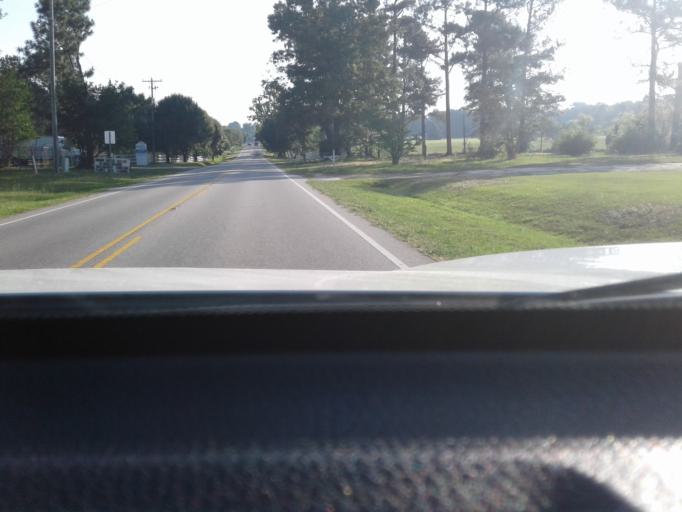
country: US
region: North Carolina
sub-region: Harnett County
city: Dunn
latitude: 35.3378
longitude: -78.5879
